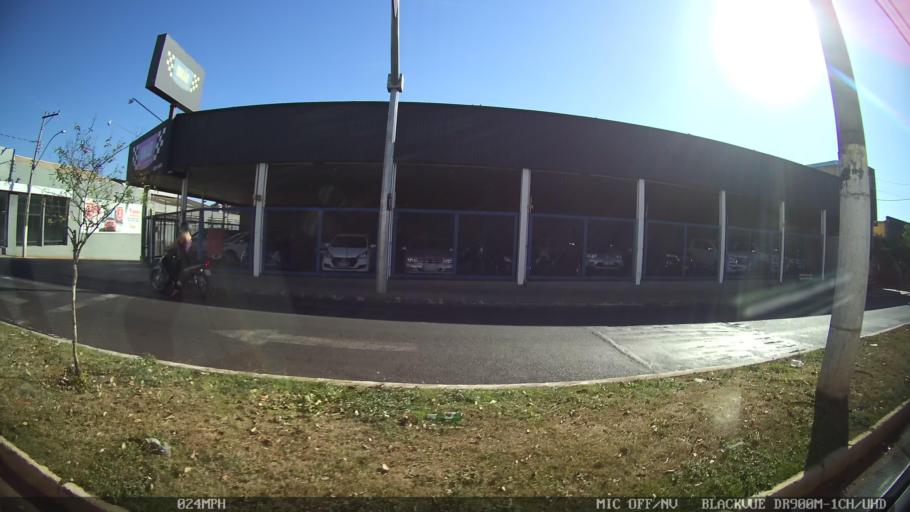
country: BR
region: Sao Paulo
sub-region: Olimpia
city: Olimpia
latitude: -20.7349
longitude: -48.9045
